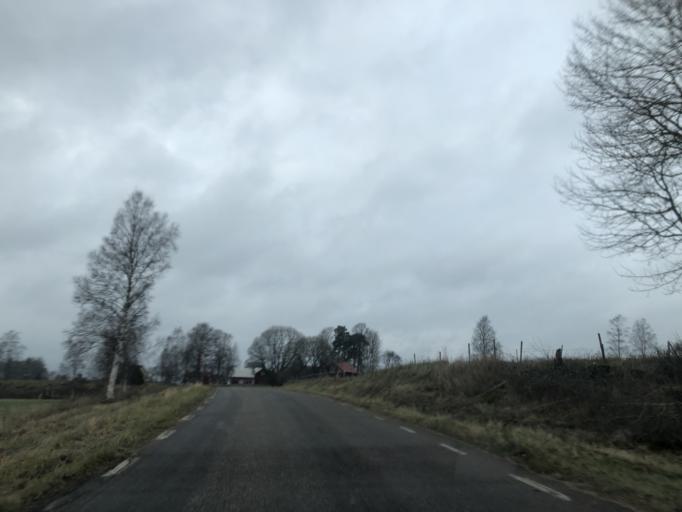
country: SE
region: Vaestra Goetaland
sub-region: Ulricehamns Kommun
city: Ulricehamn
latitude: 57.8765
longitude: 13.5383
